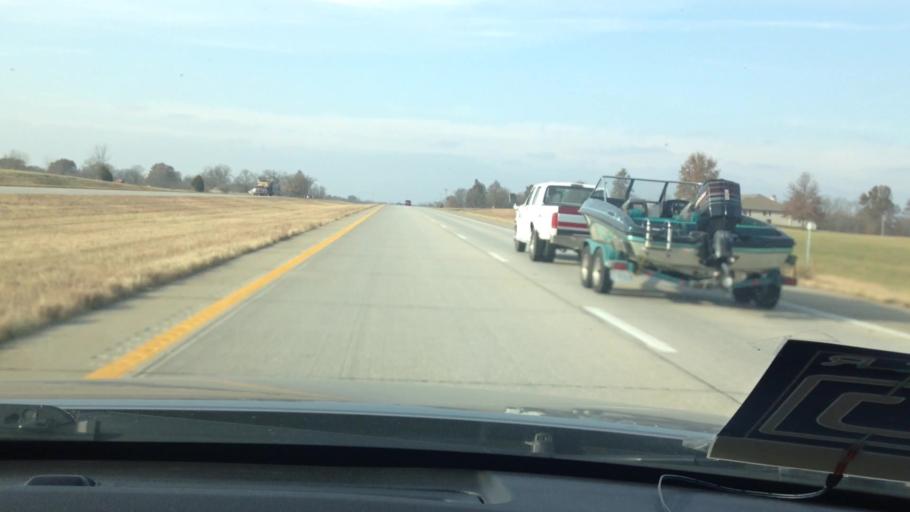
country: US
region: Missouri
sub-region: Henry County
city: Clinton
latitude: 38.4542
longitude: -93.9630
